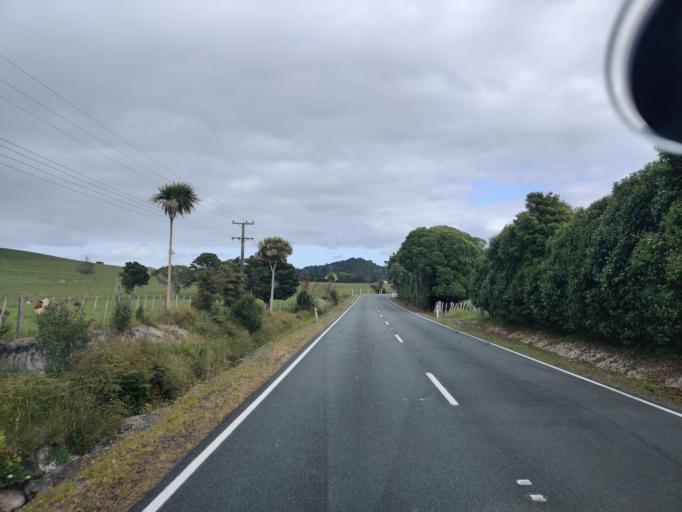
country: NZ
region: Northland
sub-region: Whangarei
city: Ngunguru
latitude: -35.5661
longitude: 174.3941
